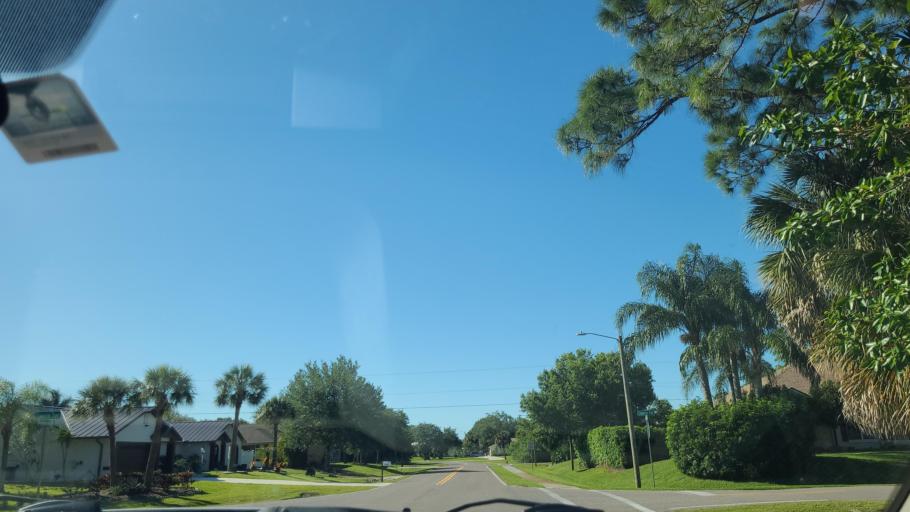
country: US
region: Florida
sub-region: Indian River County
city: Sebastian
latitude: 27.7616
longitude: -80.4875
